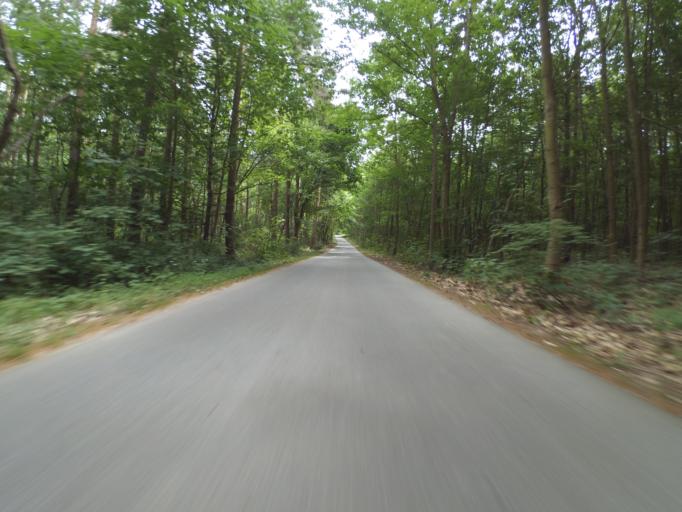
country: DE
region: Mecklenburg-Vorpommern
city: Grabowhofe
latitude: 53.5217
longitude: 12.6028
